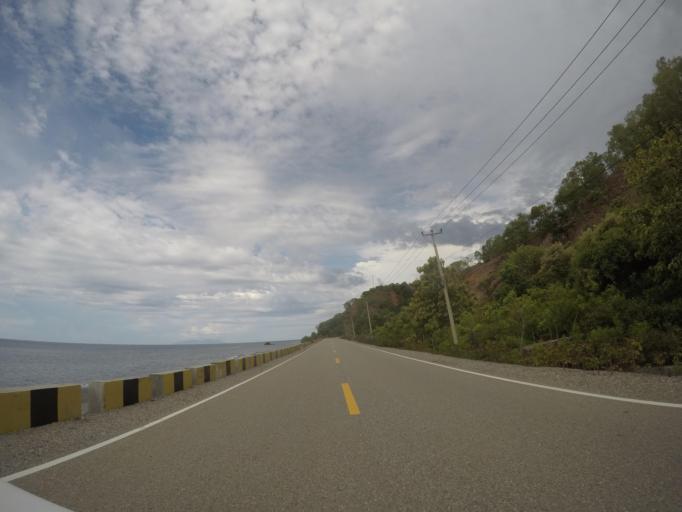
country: TL
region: Liquica
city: Maubara
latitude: -8.6141
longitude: 125.1893
